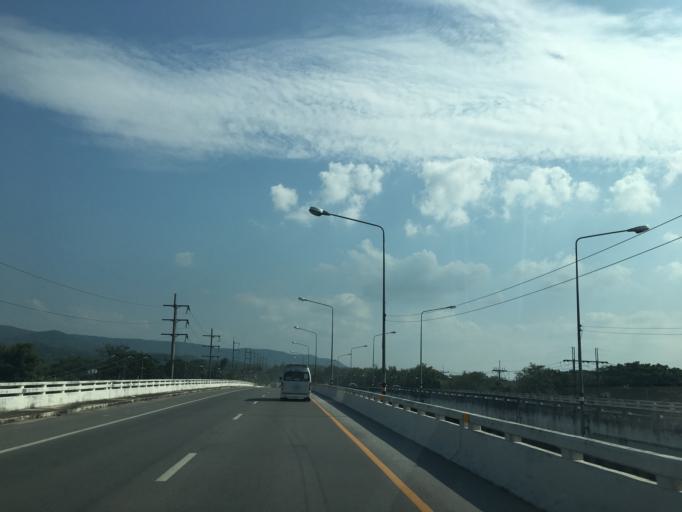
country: TH
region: Chiang Rai
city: Mae Lao
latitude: 19.7154
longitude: 99.7176
